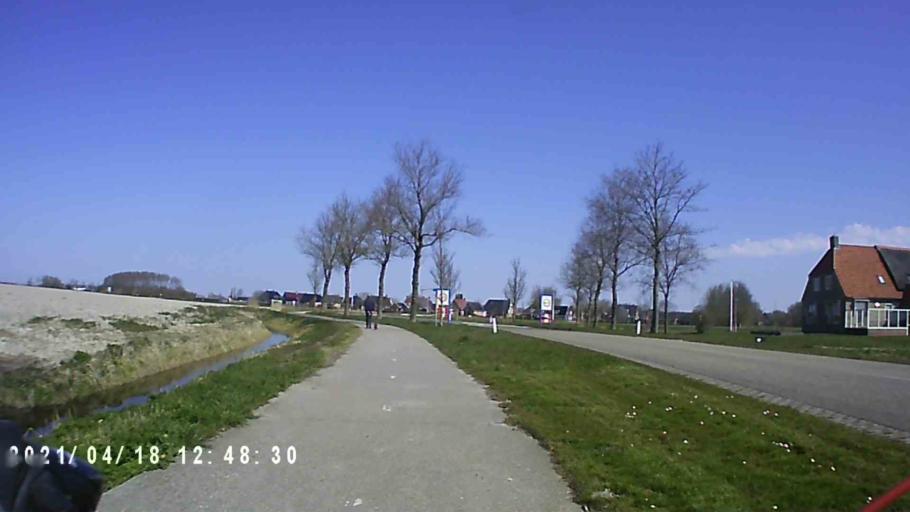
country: NL
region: Friesland
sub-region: Gemeente Dongeradeel
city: Dokkum
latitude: 53.3734
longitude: 6.0514
